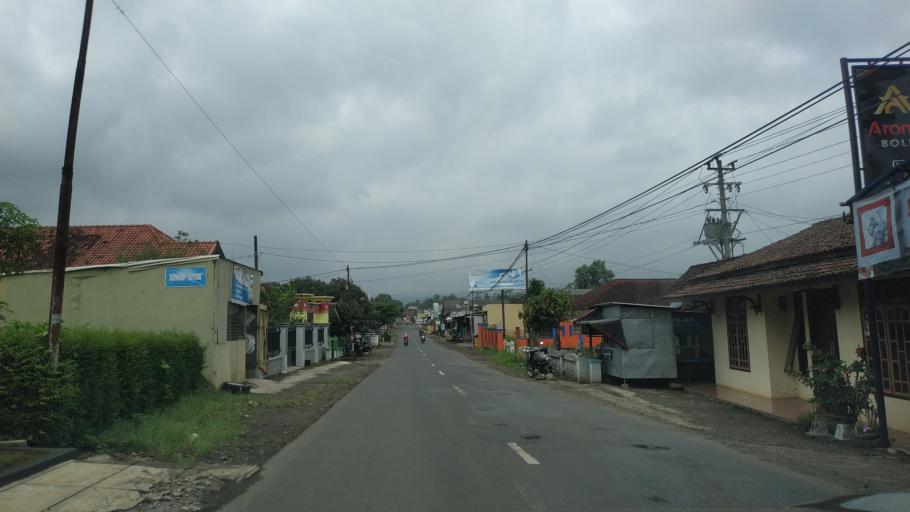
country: ID
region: Central Java
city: Weleri
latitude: -7.0782
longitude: 110.0439
